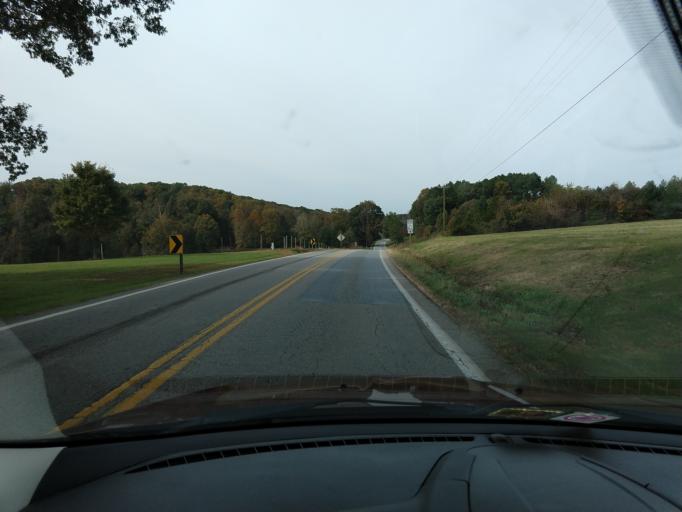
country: US
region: Virginia
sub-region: Pittsylvania County
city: Gretna
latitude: 36.9437
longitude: -79.5039
